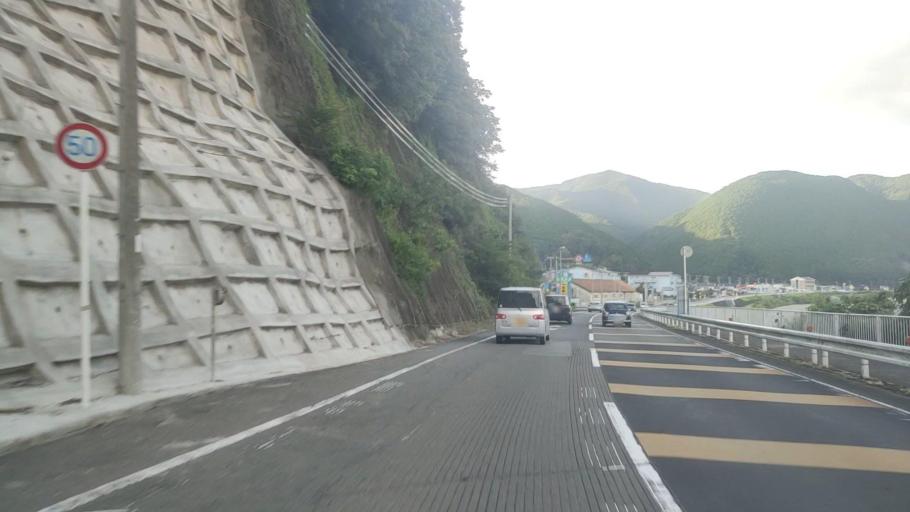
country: JP
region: Wakayama
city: Tanabe
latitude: 33.7235
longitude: 135.4811
